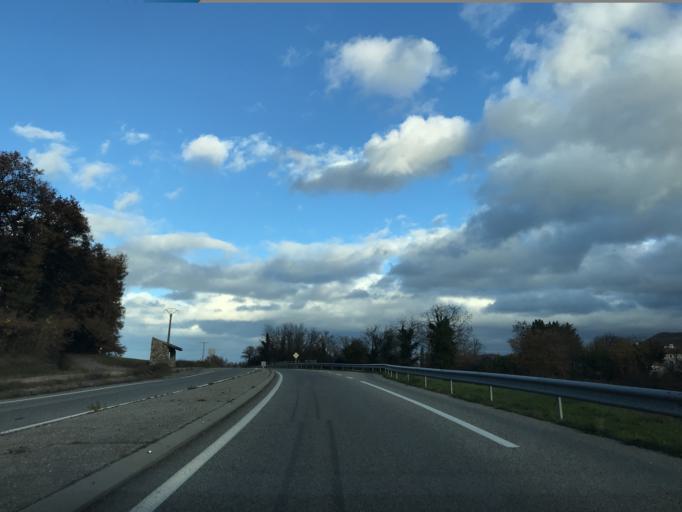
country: FR
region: Rhone-Alpes
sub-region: Departement de l'Ardeche
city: Le Pouzin
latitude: 44.7095
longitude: 4.7227
